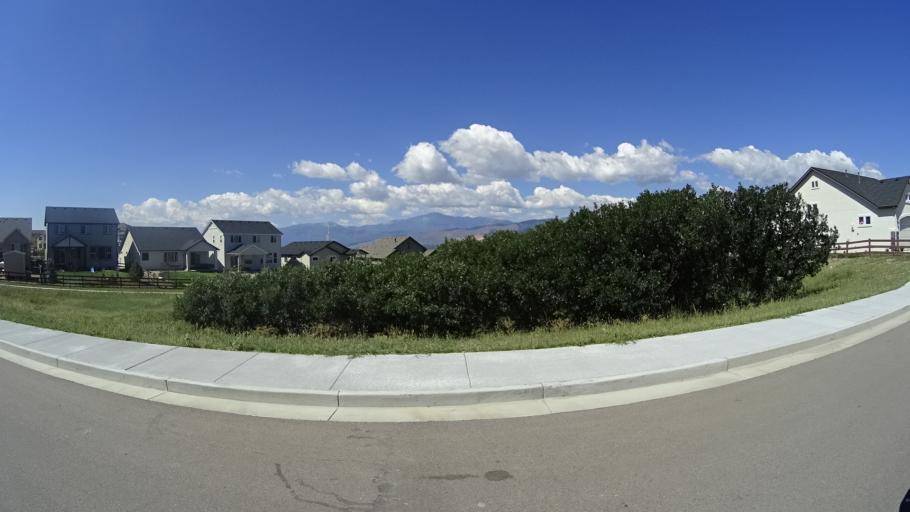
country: US
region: Colorado
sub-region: El Paso County
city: Black Forest
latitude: 38.9900
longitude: -104.7680
